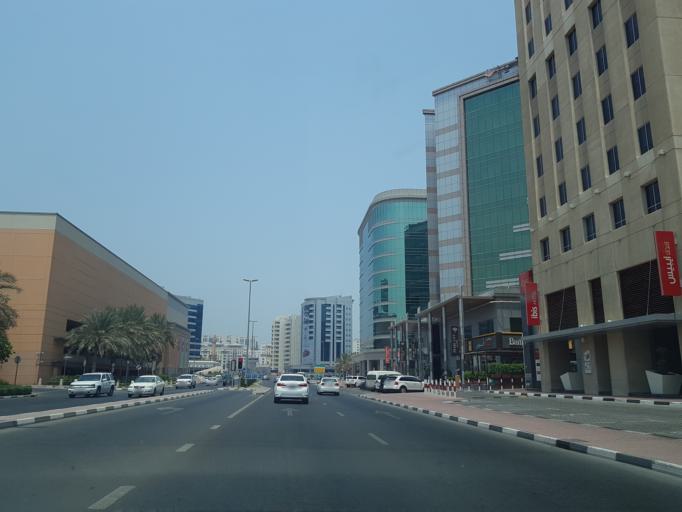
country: AE
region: Ash Shariqah
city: Sharjah
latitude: 25.2538
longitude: 55.3323
